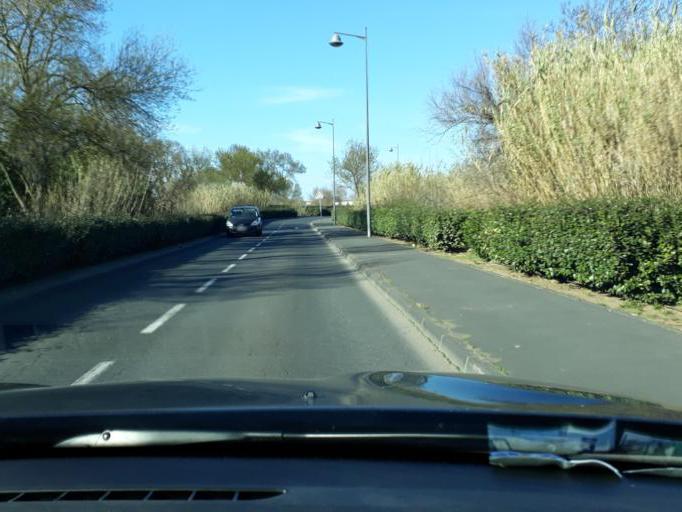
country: FR
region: Languedoc-Roussillon
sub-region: Departement de l'Herault
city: Agde
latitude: 43.3132
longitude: 3.4640
